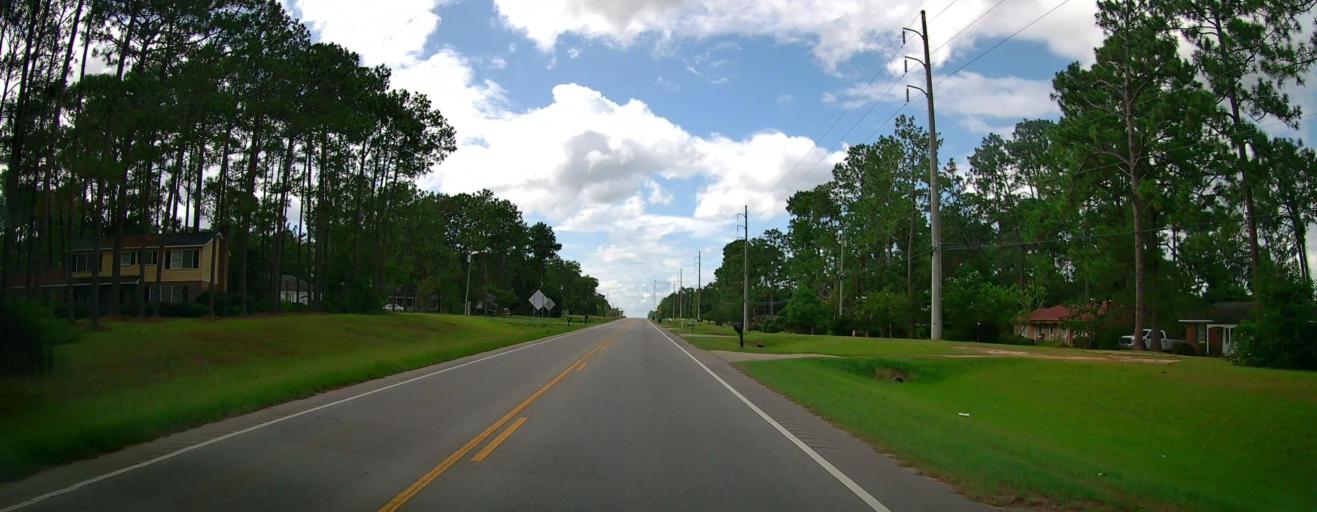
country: US
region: Georgia
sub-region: Coffee County
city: Douglas
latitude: 31.5192
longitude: -82.8712
